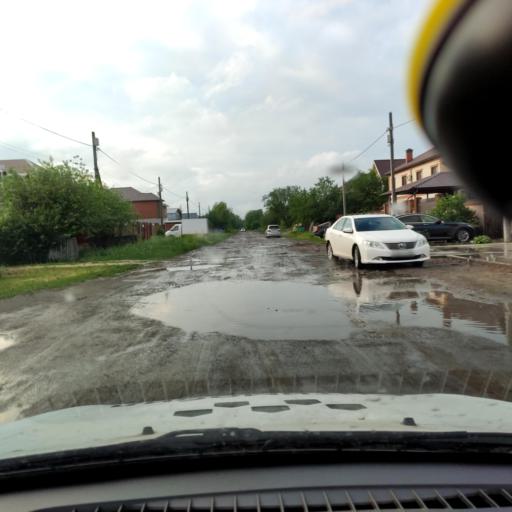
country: RU
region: Samara
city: Tol'yatti
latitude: 53.5526
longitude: 49.4078
